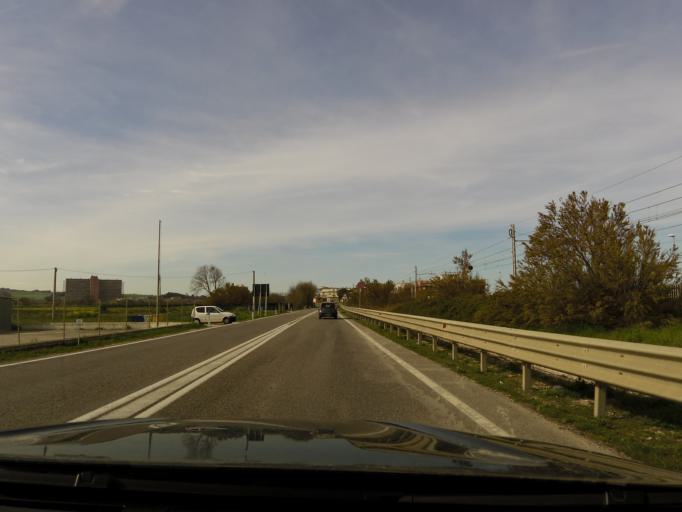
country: IT
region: The Marches
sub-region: Provincia di Macerata
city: Porto Recanati
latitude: 43.4094
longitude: 13.6761
